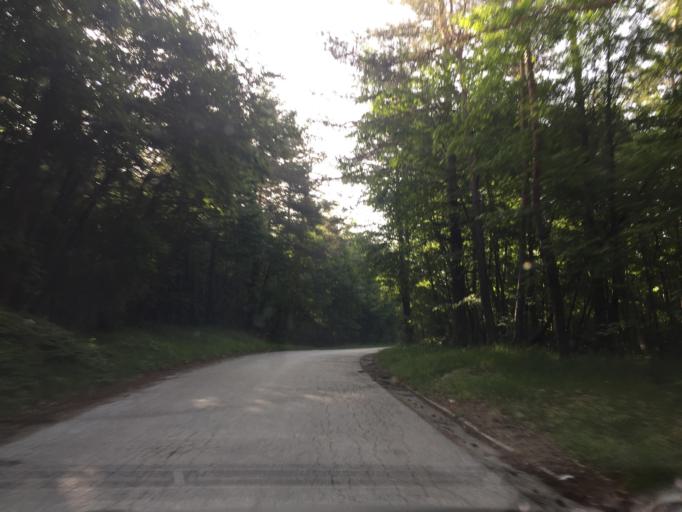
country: HR
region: Istarska
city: Buzet
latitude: 45.4773
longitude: 14.0738
